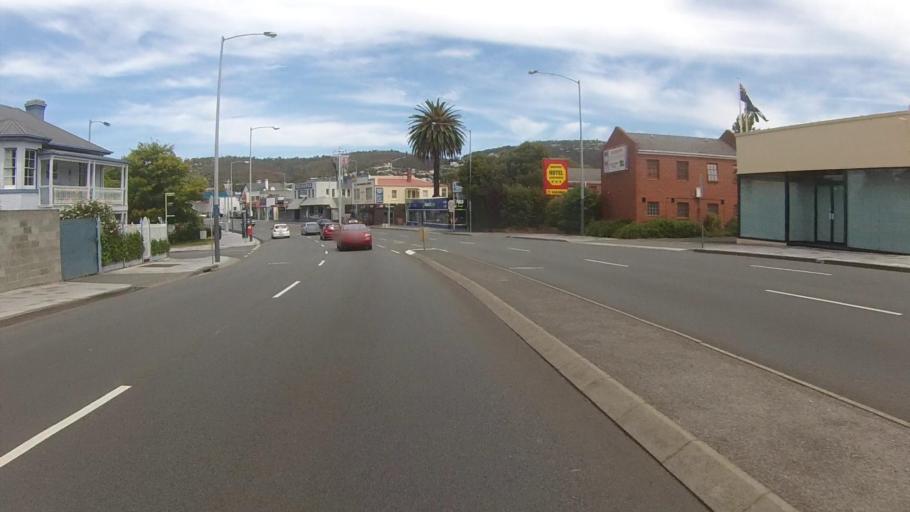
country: AU
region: Tasmania
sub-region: Hobart
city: Sandy Bay
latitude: -42.8925
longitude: 147.3261
